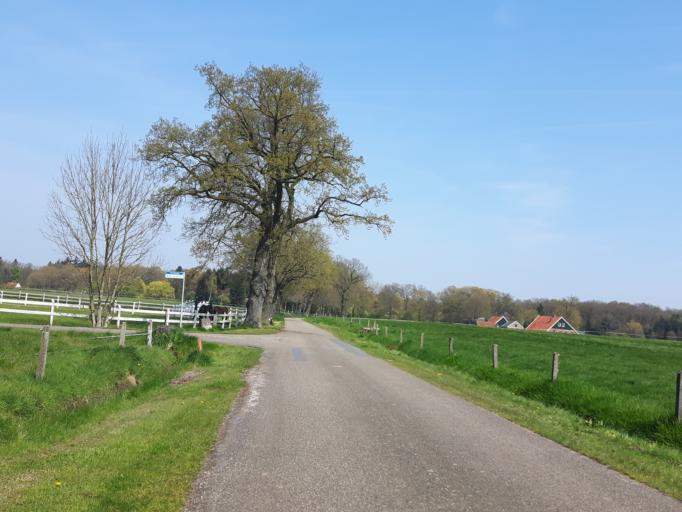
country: NL
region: Overijssel
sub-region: Gemeente Haaksbergen
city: Haaksbergen
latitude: 52.1468
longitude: 6.8200
